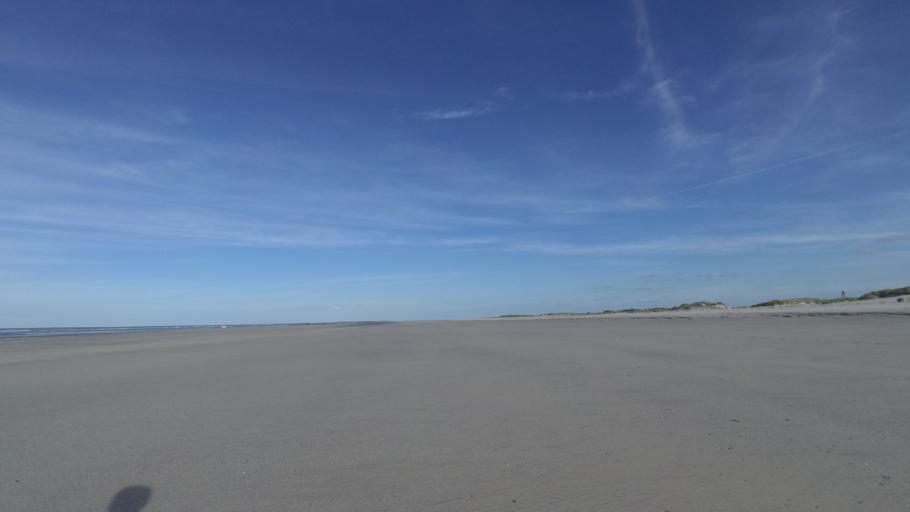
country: NL
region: Friesland
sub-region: Gemeente Dongeradeel
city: Ternaard
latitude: 53.4681
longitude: 5.9212
